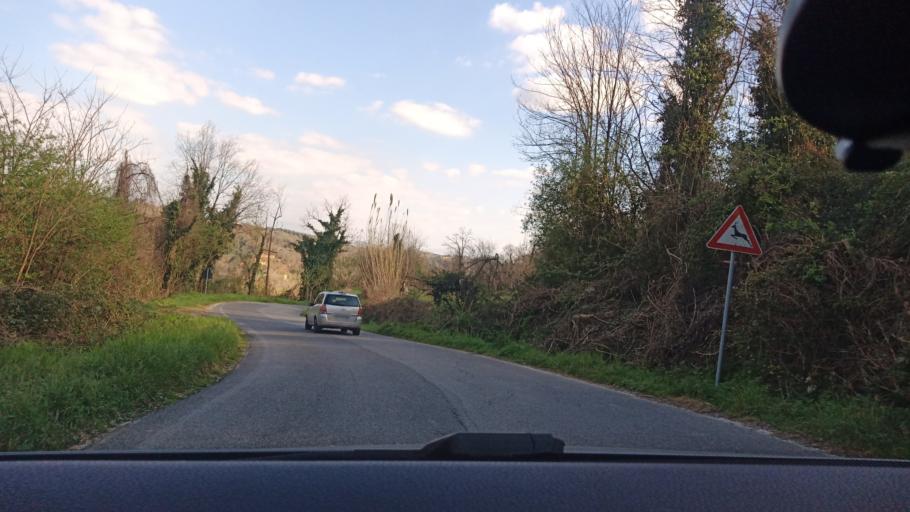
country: IT
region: Latium
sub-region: Citta metropolitana di Roma Capitale
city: Torrita Tiberina
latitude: 42.2394
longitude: 12.6228
